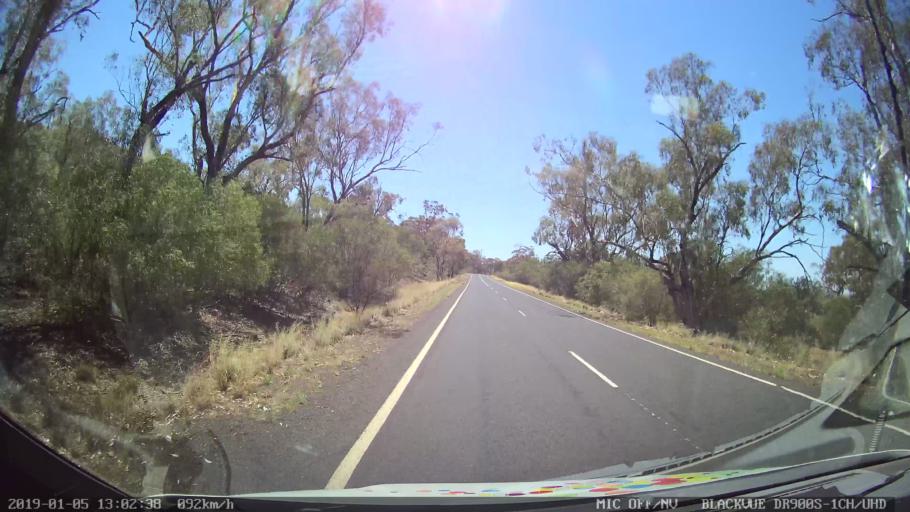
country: AU
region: New South Wales
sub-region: Gunnedah
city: Gunnedah
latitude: -31.1139
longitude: 149.8145
